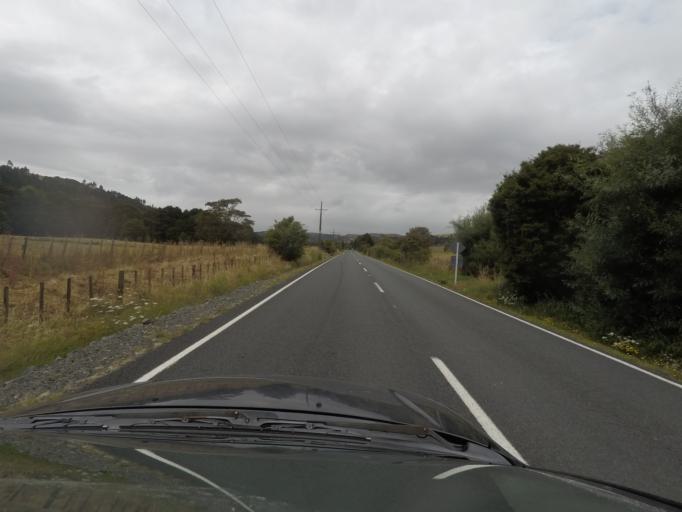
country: NZ
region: Auckland
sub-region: Auckland
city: Wellsford
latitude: -36.2923
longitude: 174.6235
